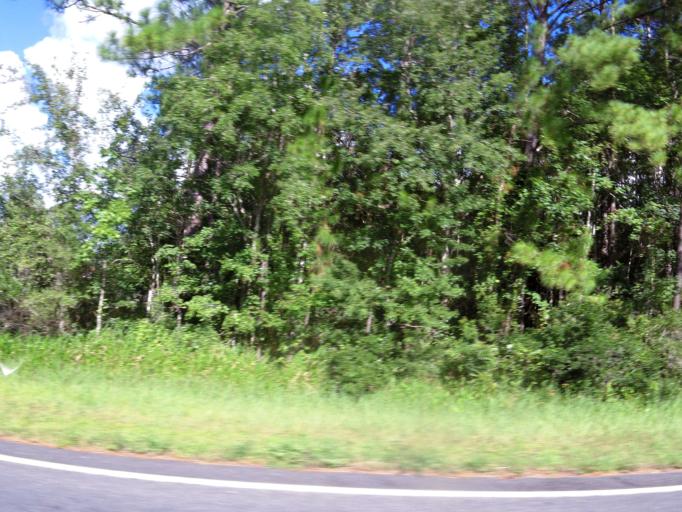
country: US
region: Georgia
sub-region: Camden County
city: Kingsland
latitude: 30.8540
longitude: -81.7010
